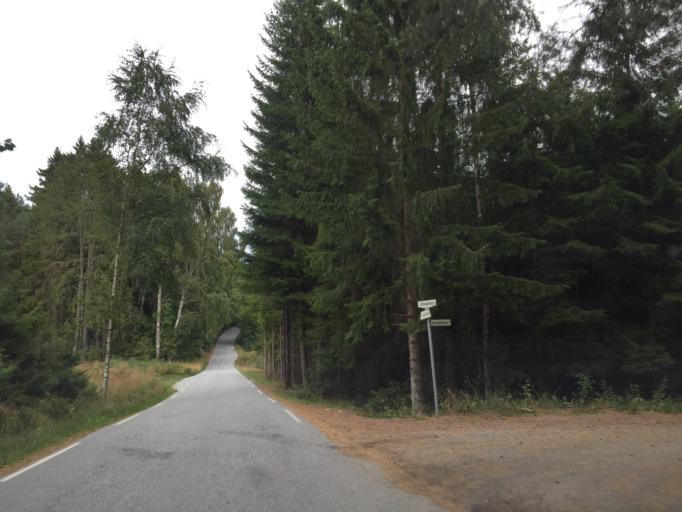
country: NO
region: Ostfold
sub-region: Hvaler
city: Skjaerhalden
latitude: 59.0538
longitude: 11.0529
